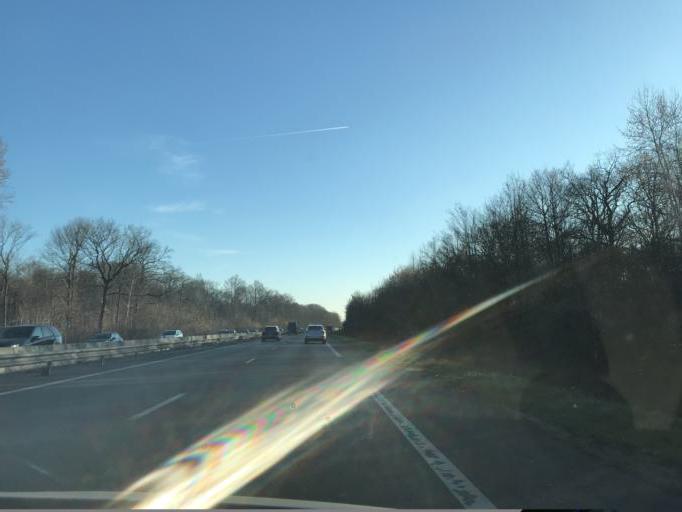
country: FR
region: Ile-de-France
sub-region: Departement de Seine-et-Marne
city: Lesigny
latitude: 48.7589
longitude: 2.6155
